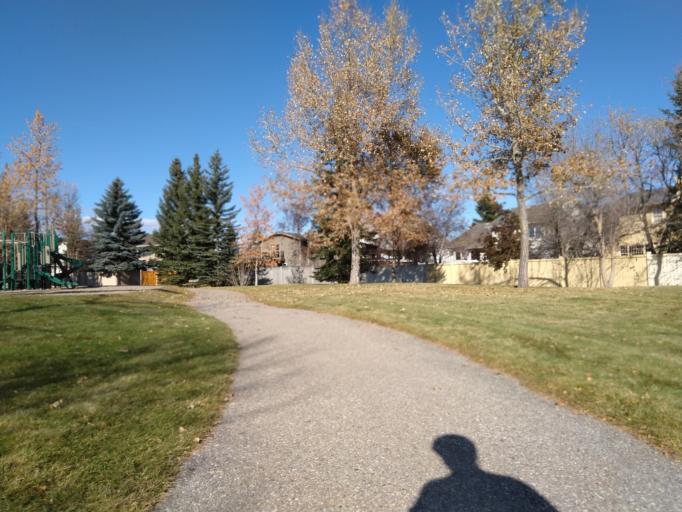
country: CA
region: Alberta
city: Calgary
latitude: 51.1363
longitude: -114.1538
